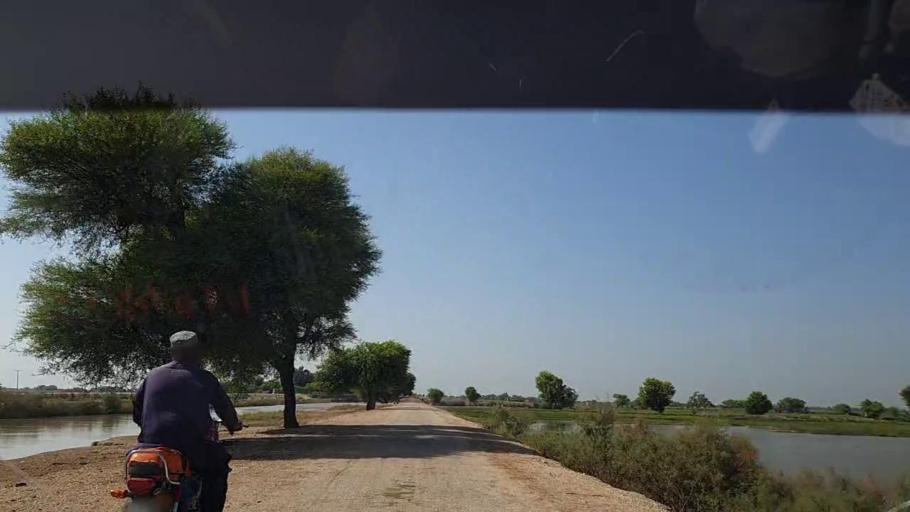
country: PK
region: Sindh
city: Ghauspur
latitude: 28.1987
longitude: 69.0437
